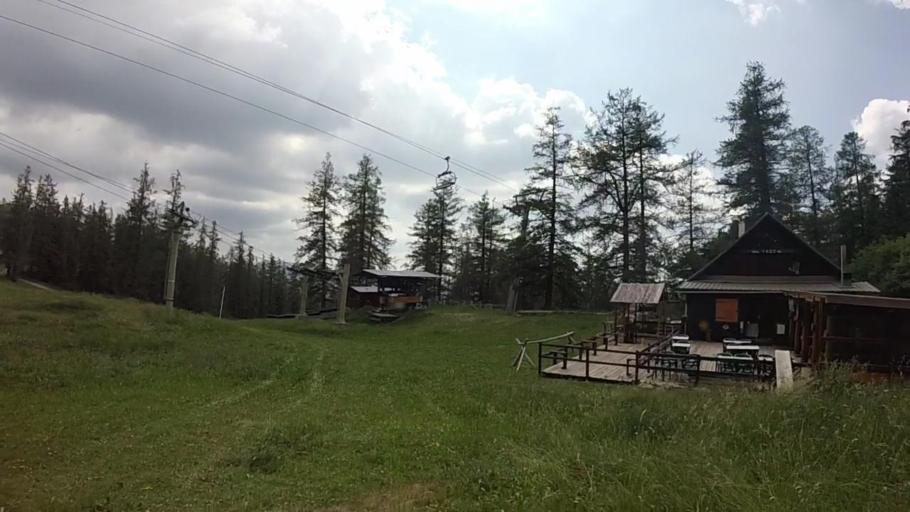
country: FR
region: Provence-Alpes-Cote d'Azur
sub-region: Departement des Alpes-de-Haute-Provence
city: Seyne-les-Alpes
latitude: 44.4068
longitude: 6.3632
